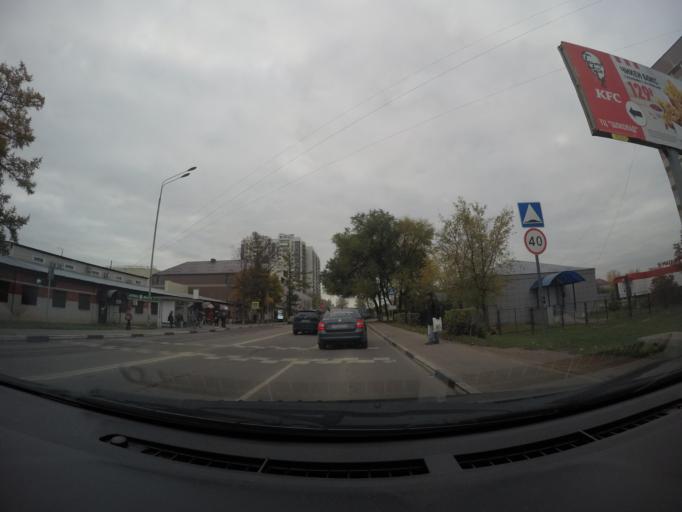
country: RU
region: Moskovskaya
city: Staraya Kupavna
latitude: 55.8035
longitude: 38.1811
